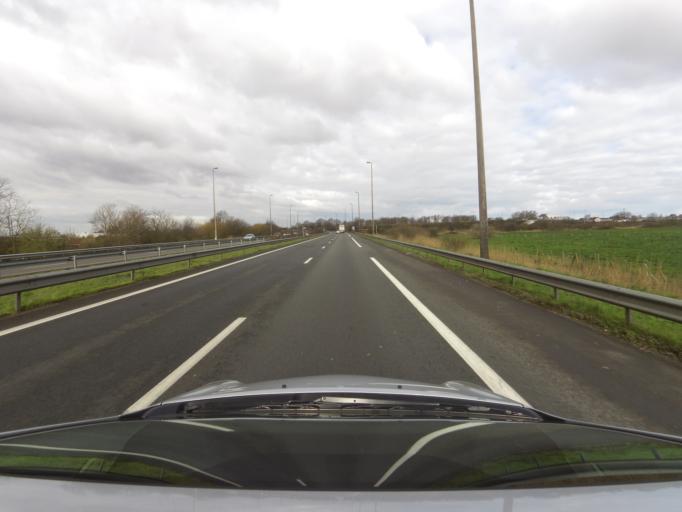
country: FR
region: Nord-Pas-de-Calais
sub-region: Departement du Pas-de-Calais
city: Coulogne
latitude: 50.9348
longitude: 1.8814
